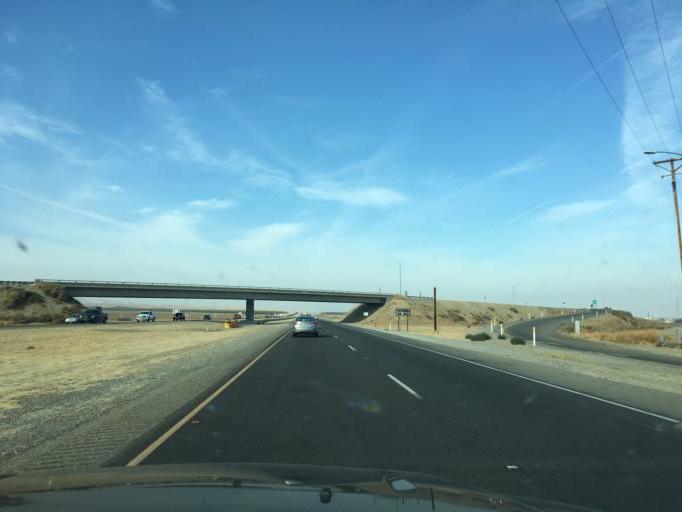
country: US
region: California
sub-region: Fresno County
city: San Joaquin
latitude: 36.4348
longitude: -120.3932
